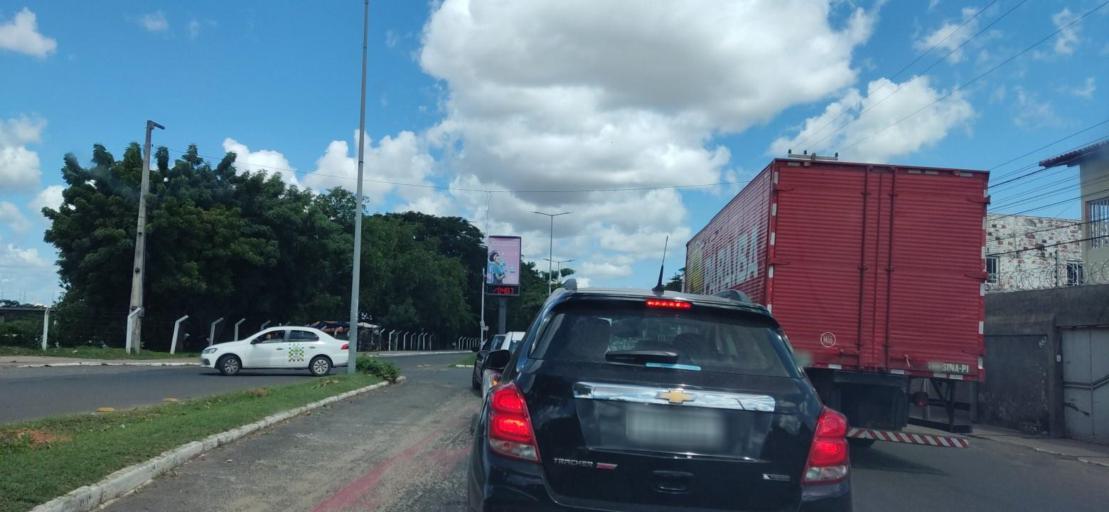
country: BR
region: Maranhao
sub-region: Timon
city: Timon
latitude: -5.0933
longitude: -42.8222
